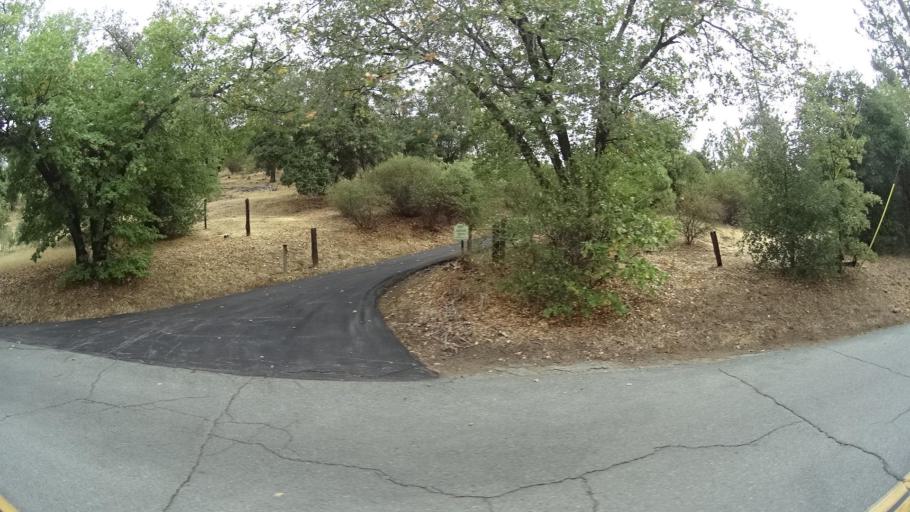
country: US
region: California
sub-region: San Diego County
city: Julian
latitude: 33.0549
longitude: -116.6014
